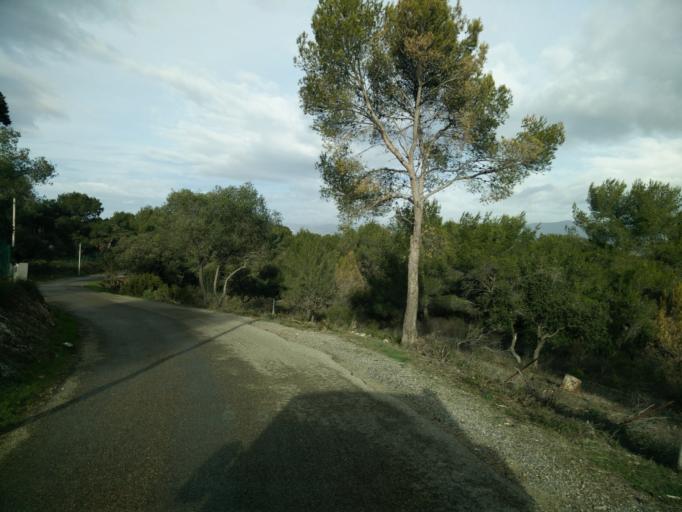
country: FR
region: Provence-Alpes-Cote d'Azur
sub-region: Departement du Var
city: Six-Fours-les-Plages
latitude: 43.0674
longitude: 5.8270
